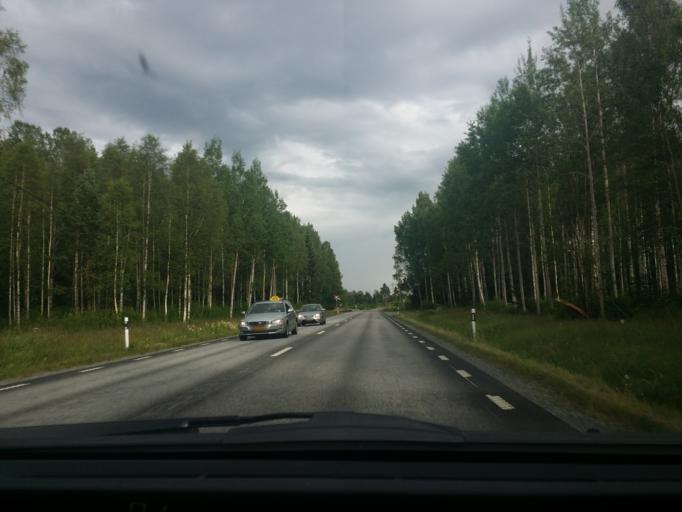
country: SE
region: OErebro
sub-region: Nora Kommun
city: Nora
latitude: 59.4807
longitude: 15.0867
